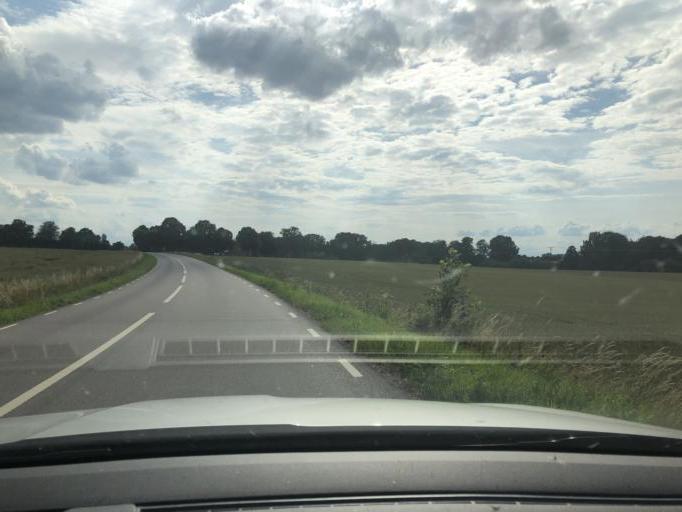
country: SE
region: OEstergoetland
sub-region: Odeshogs Kommun
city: OEdeshoeg
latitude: 58.2402
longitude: 14.7061
